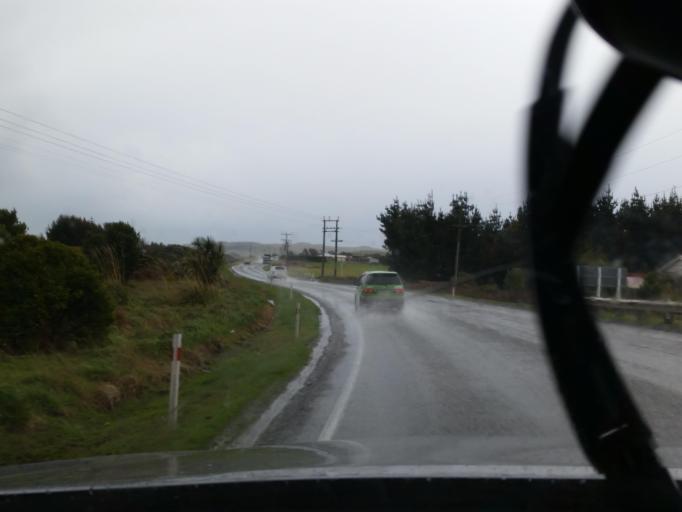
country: NZ
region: Southland
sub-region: Invercargill City
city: Bluff
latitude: -46.5379
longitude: 168.3030
